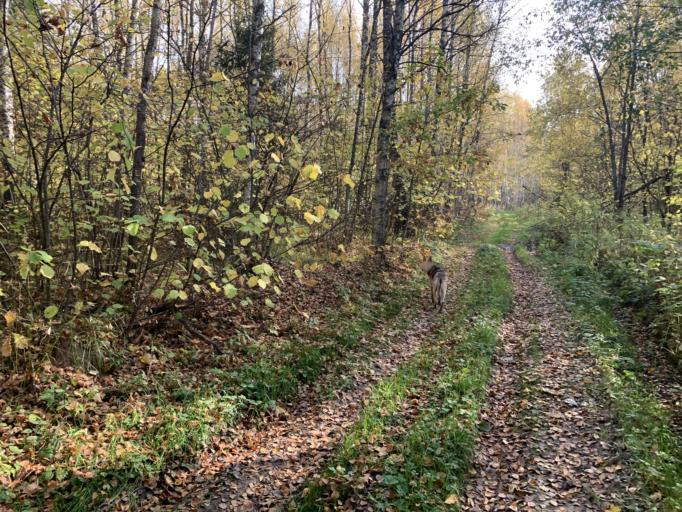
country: RU
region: Jaroslavl
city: Porech'ye-Rybnoye
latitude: 57.0024
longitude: 39.4057
